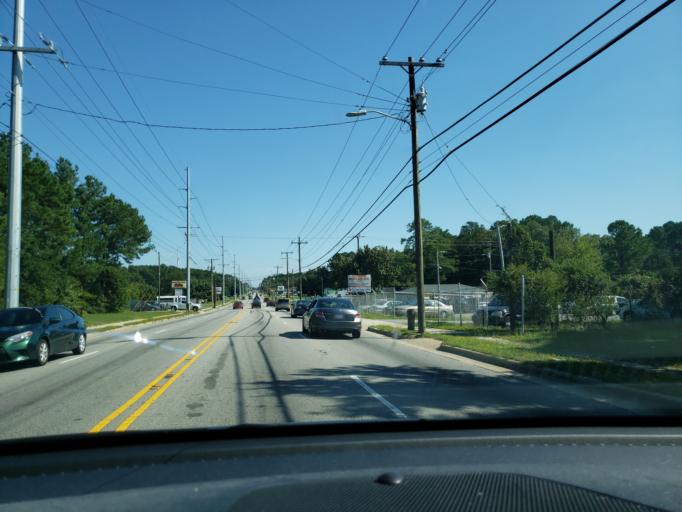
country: US
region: North Carolina
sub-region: Cumberland County
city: Fayetteville
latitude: 35.0938
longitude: -78.9127
